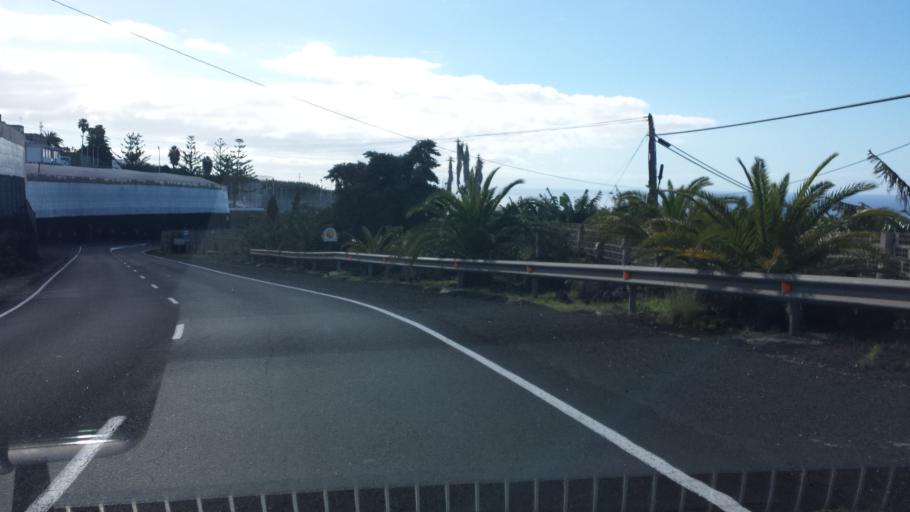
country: ES
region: Canary Islands
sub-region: Provincia de Santa Cruz de Tenerife
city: Tazacorte
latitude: 28.5996
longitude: -17.9102
